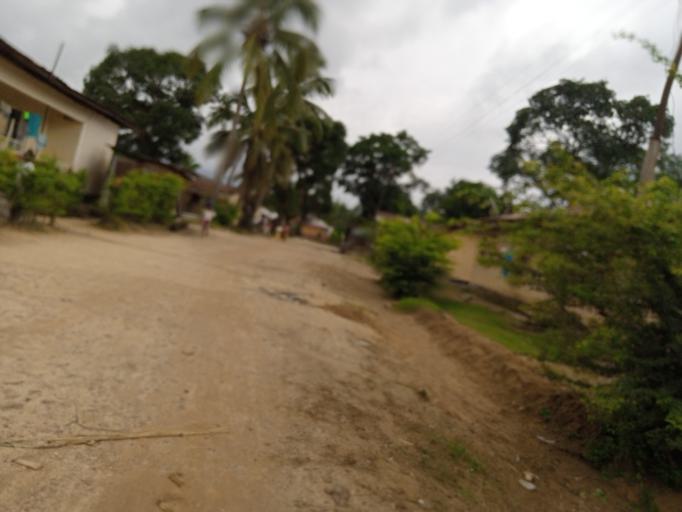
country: SL
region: Eastern Province
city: Kenema
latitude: 7.8768
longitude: -11.1793
